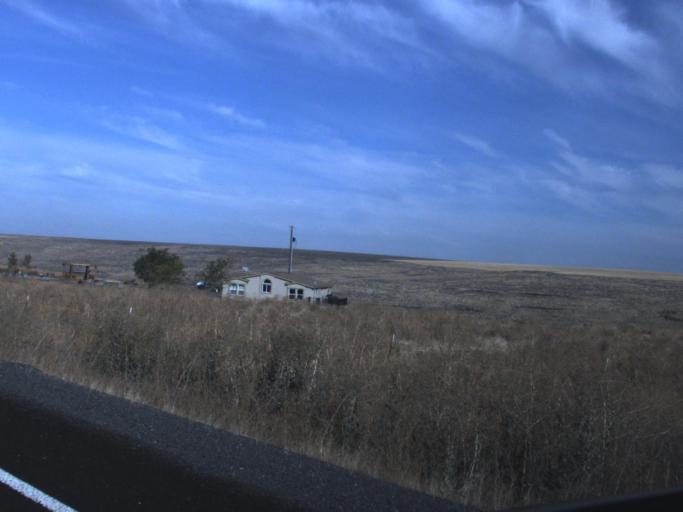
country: US
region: Washington
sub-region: Franklin County
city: Connell
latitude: 46.6291
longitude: -118.7260
